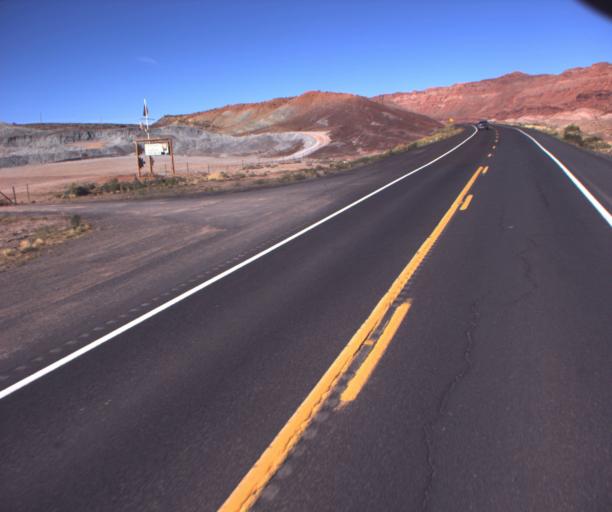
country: US
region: Arizona
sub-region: Coconino County
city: Tuba City
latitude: 36.1916
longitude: -111.3932
